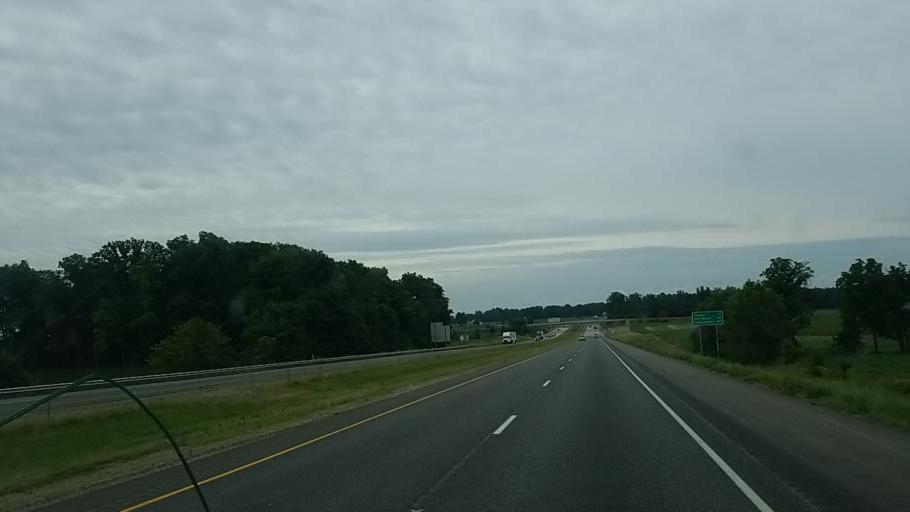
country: US
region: Indiana
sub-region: DeKalb County
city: Waterloo
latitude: 41.4304
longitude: -85.0536
